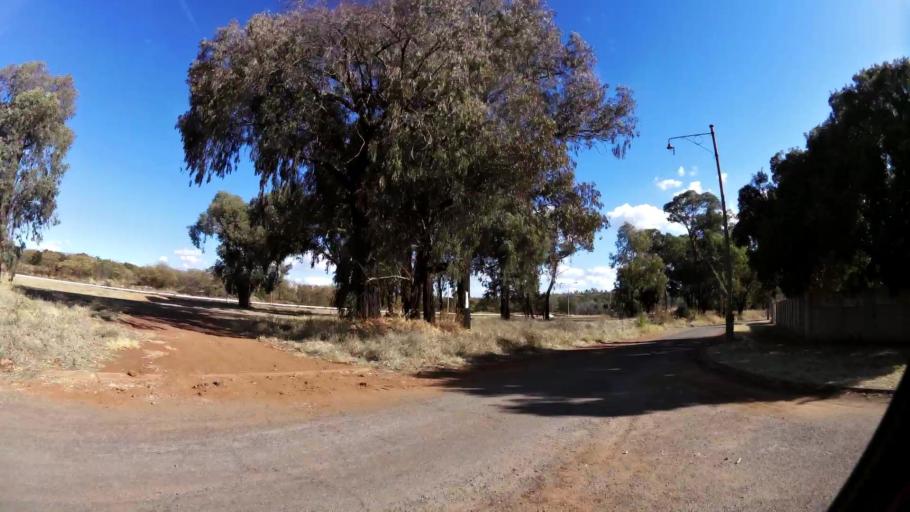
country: ZA
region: Gauteng
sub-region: West Rand District Municipality
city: Carletonville
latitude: -26.3754
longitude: 27.3998
